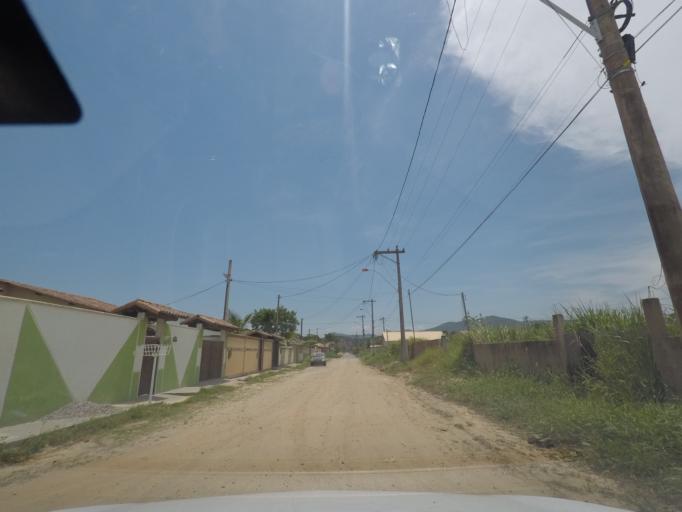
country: BR
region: Rio de Janeiro
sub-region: Marica
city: Marica
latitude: -22.9544
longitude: -42.9541
